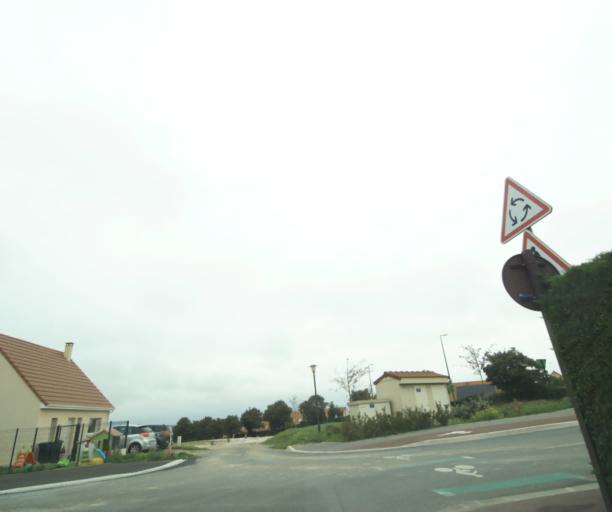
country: FR
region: Nord-Pas-de-Calais
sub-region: Departement du Pas-de-Calais
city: Etaples
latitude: 50.5149
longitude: 1.6541
